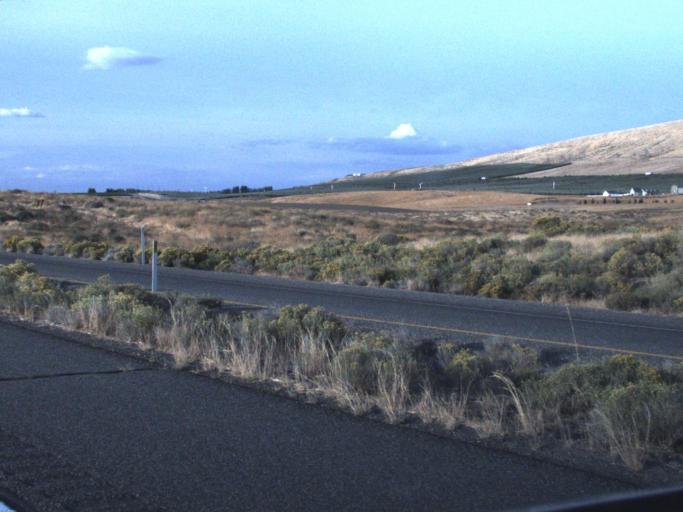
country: US
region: Washington
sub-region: Benton County
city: West Richland
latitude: 46.2197
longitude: -119.3491
